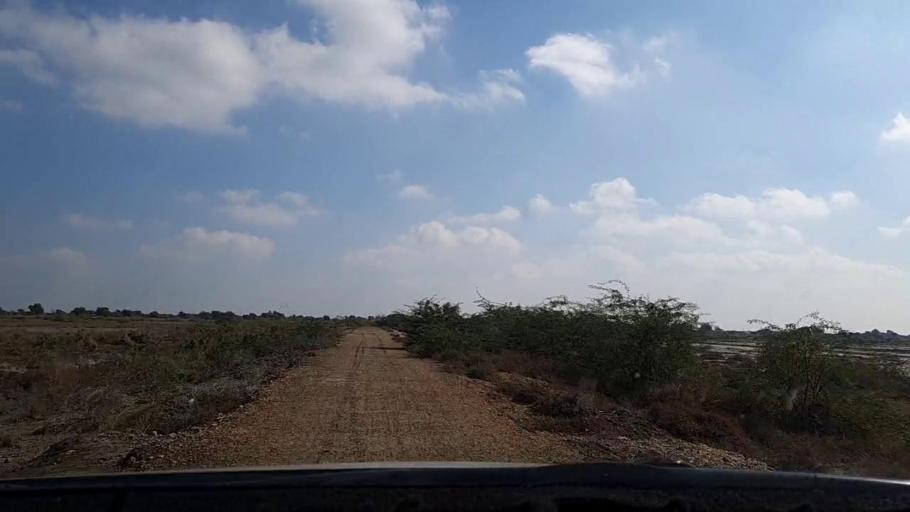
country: PK
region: Sindh
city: Pithoro
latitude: 25.7213
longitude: 69.2947
